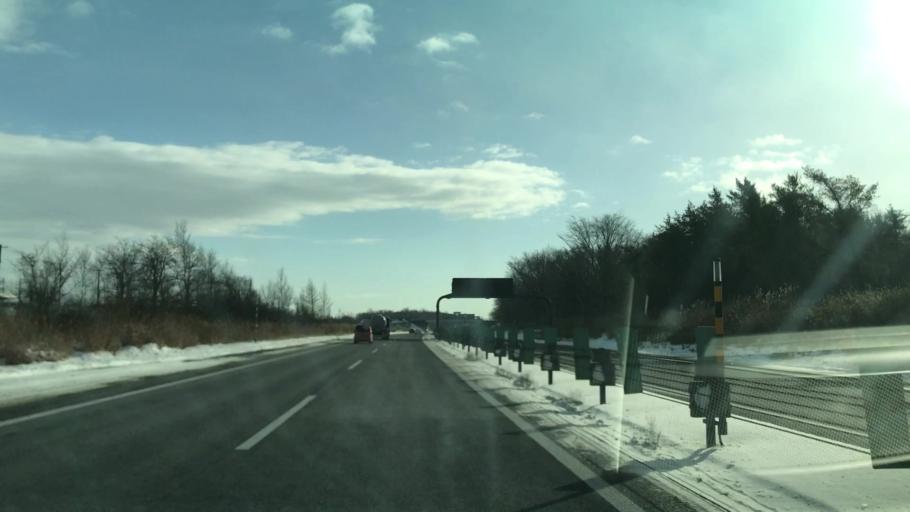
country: JP
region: Hokkaido
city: Chitose
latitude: 42.8418
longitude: 141.5955
